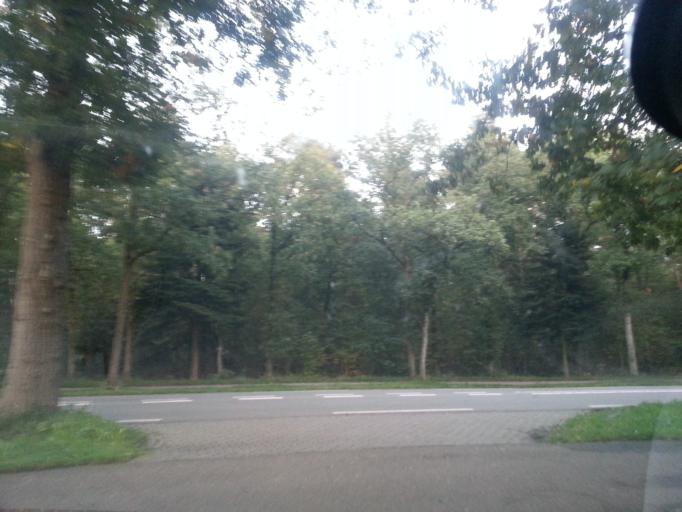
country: NL
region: Utrecht
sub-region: Gemeente Zeist
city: Zeist
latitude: 52.0883
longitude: 5.2628
